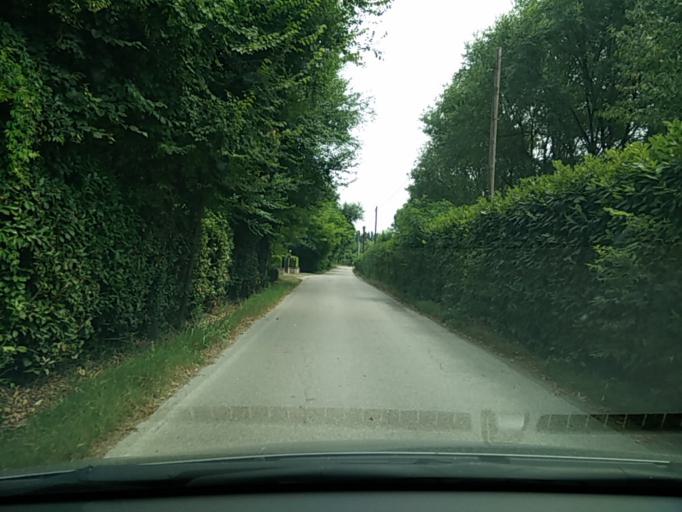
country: IT
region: Veneto
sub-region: Provincia di Treviso
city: Casier
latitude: 45.6472
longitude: 12.2845
